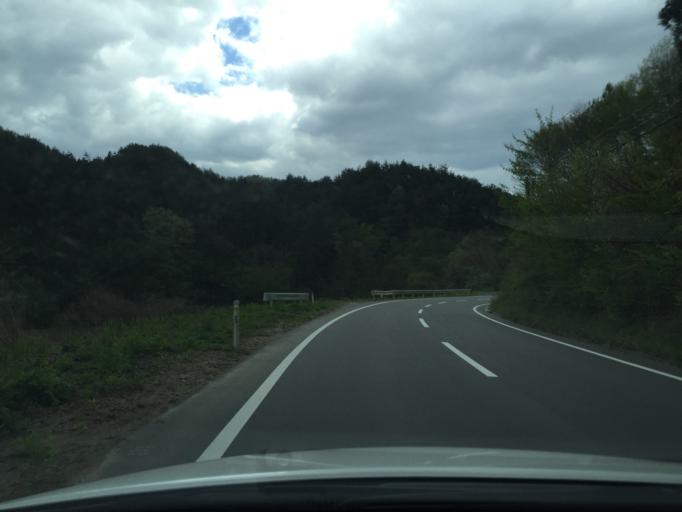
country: JP
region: Fukushima
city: Yanagawamachi-saiwaicho
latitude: 37.7296
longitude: 140.7339
